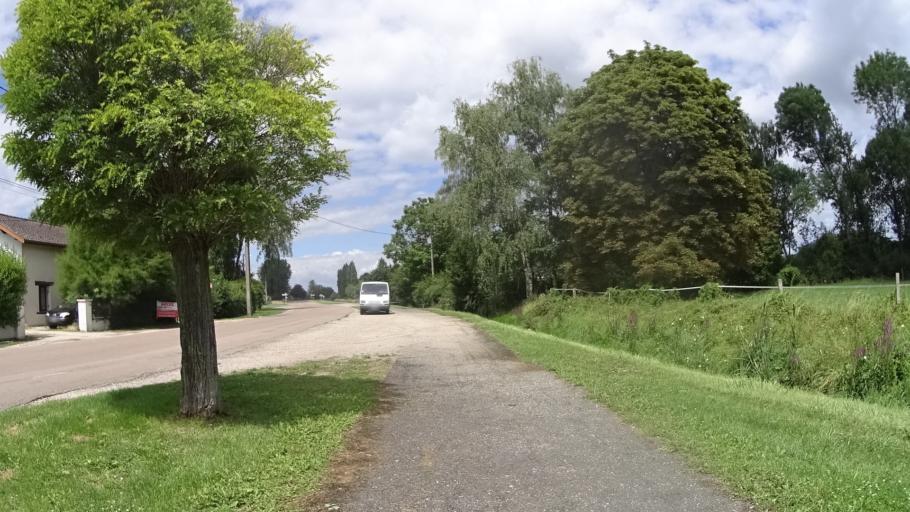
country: FR
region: Champagne-Ardenne
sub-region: Departement de la Haute-Marne
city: Montier-en-Der
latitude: 48.4749
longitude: 4.7635
